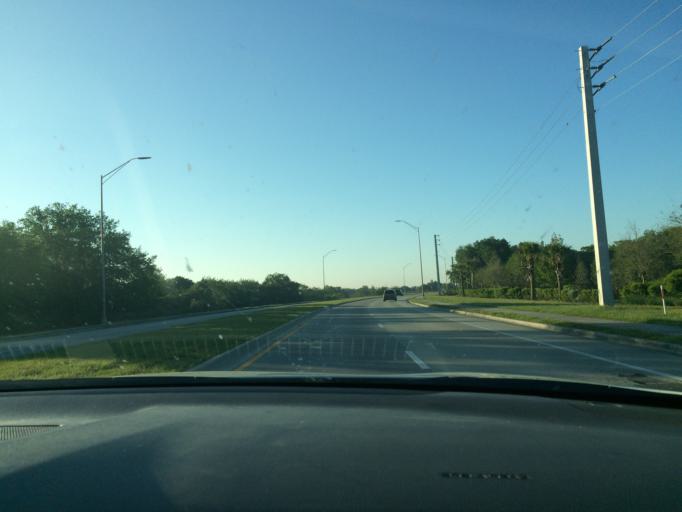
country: US
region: Florida
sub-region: Manatee County
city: Ellenton
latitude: 27.4702
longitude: -82.4322
